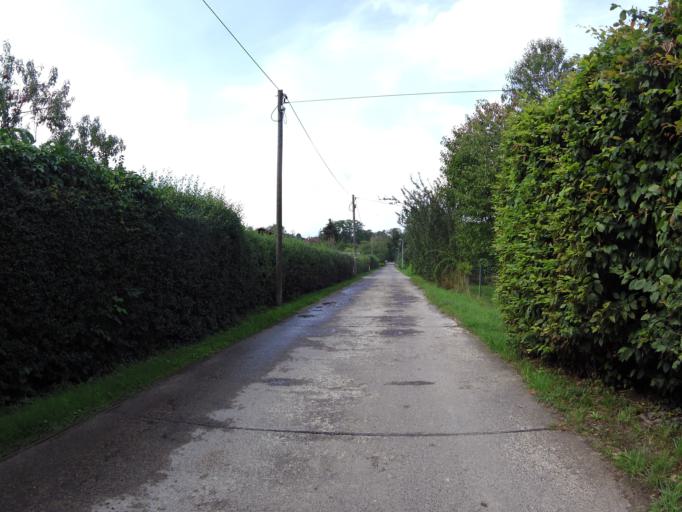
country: DE
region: Brandenburg
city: Storkow
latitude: 52.2591
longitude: 13.9493
